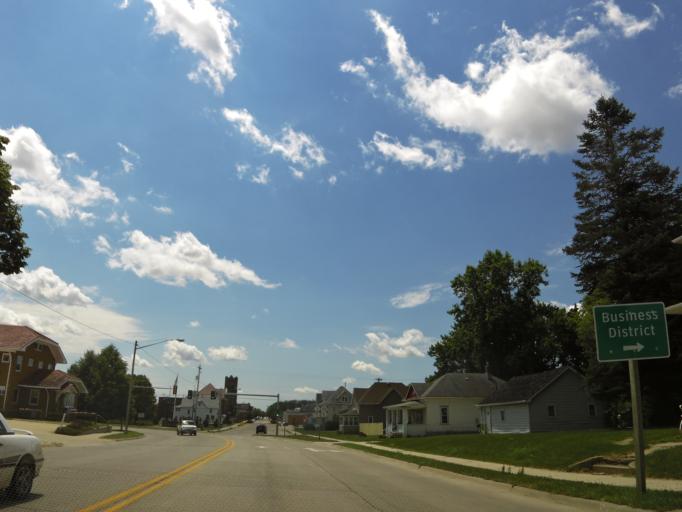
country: US
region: Iowa
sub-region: Fayette County
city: Oelwein
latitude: 42.6824
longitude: -91.9135
